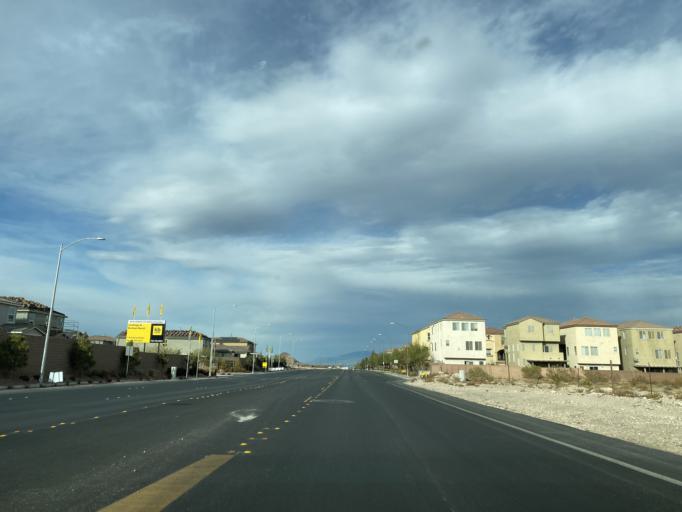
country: US
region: Nevada
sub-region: Clark County
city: Enterprise
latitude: 36.0131
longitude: -115.2982
